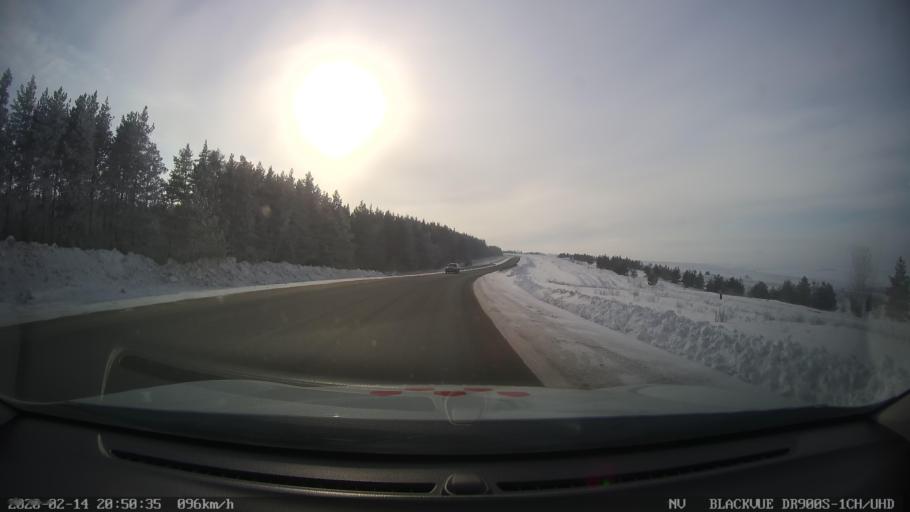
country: RU
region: Tatarstan
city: Kuybyshevskiy Zaton
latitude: 55.2251
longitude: 49.2331
